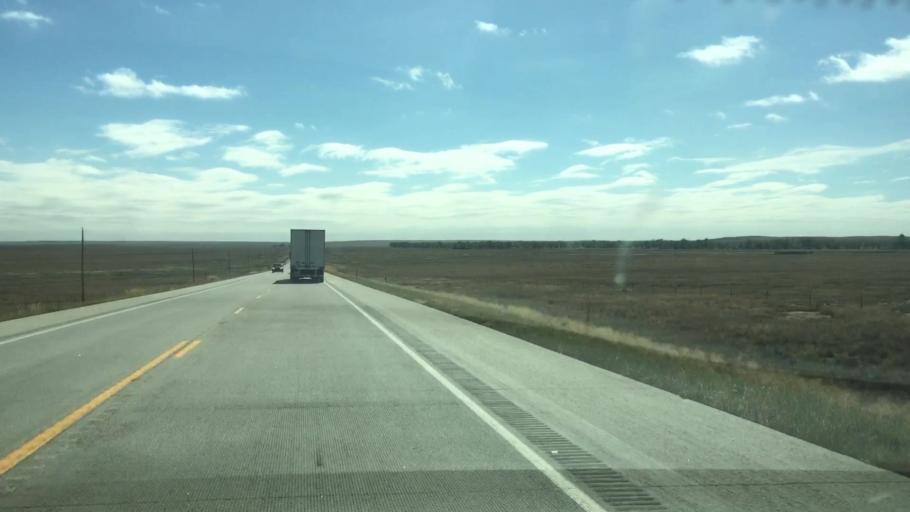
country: US
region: Colorado
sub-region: Lincoln County
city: Hugo
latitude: 39.0735
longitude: -103.3785
